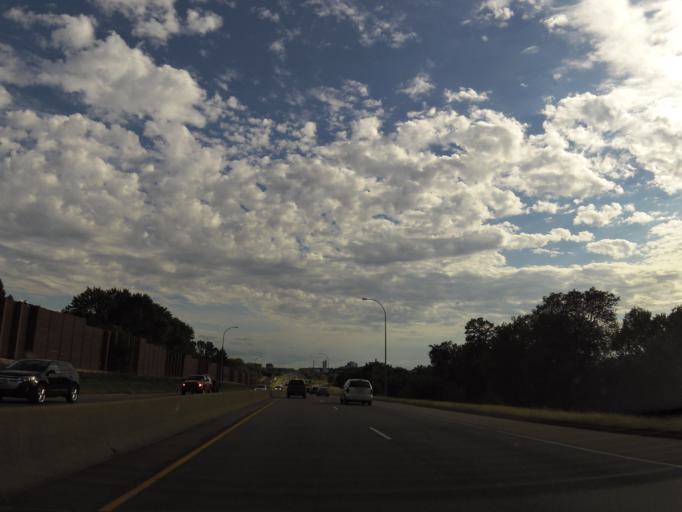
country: US
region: Minnesota
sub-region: Hennepin County
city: New Hope
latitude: 45.0009
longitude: -93.4010
